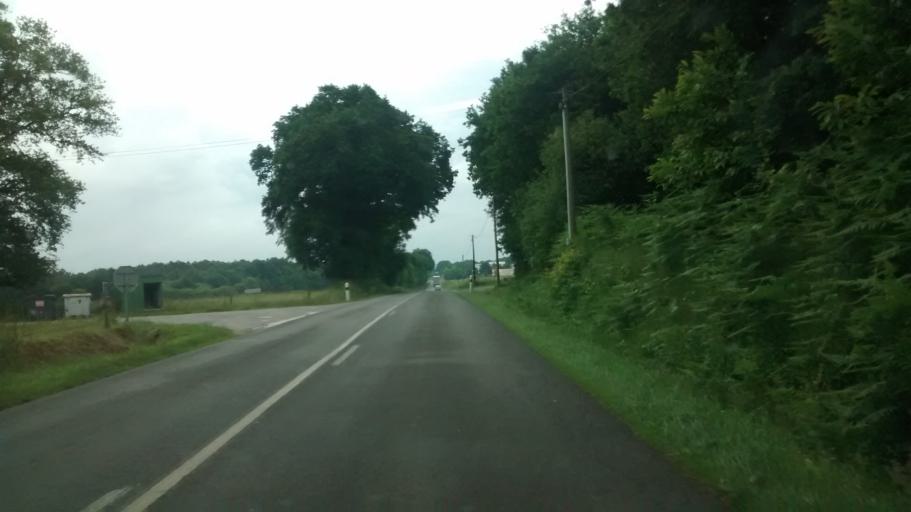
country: FR
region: Brittany
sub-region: Departement du Morbihan
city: Serent
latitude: 47.8185
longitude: -2.4487
